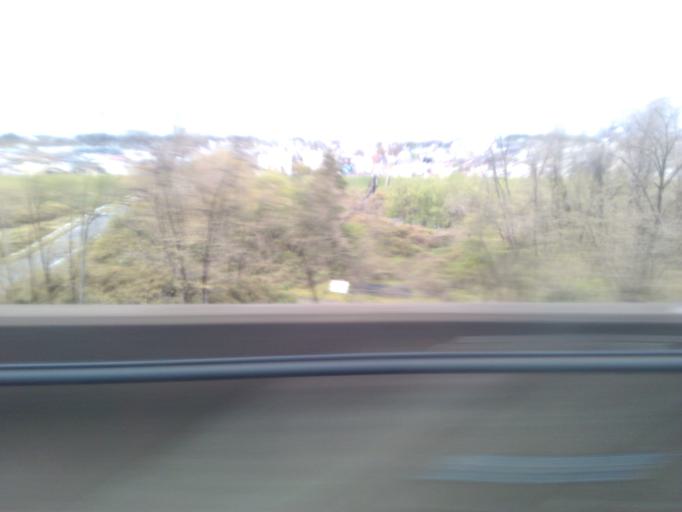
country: JP
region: Fukushima
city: Koriyama
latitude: 37.3559
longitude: 140.3739
